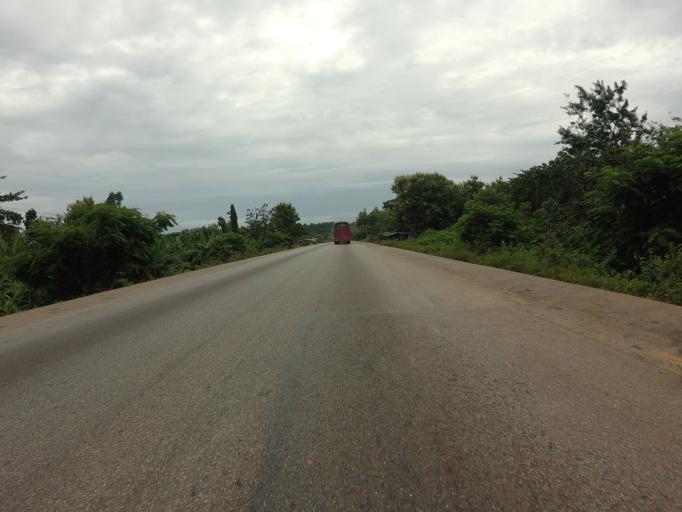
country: GH
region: Ashanti
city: Agogo
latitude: 6.6008
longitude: -0.9872
